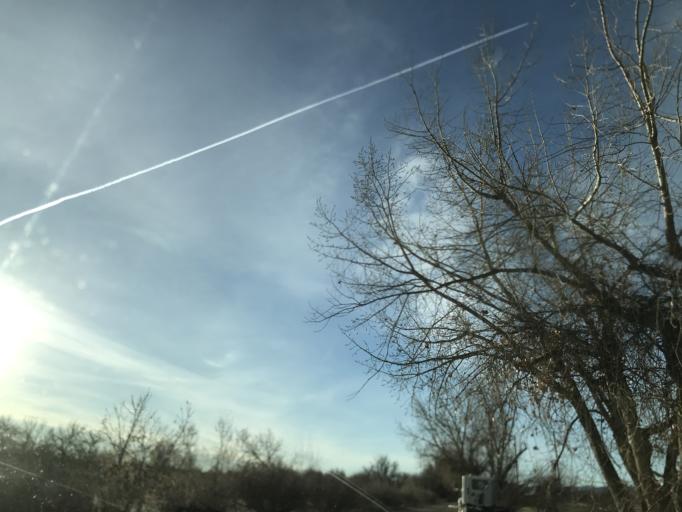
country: US
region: Colorado
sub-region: Arapahoe County
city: Littleton
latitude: 39.6113
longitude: -105.0261
